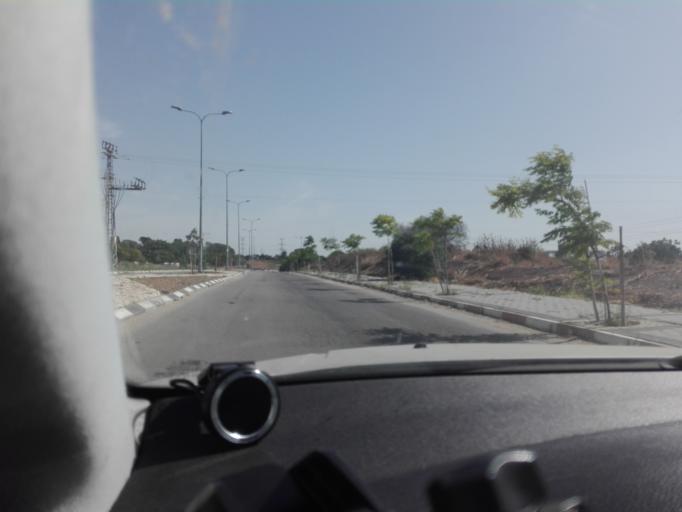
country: IL
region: Central District
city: Bene 'Ayish
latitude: 31.7203
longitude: 34.7565
